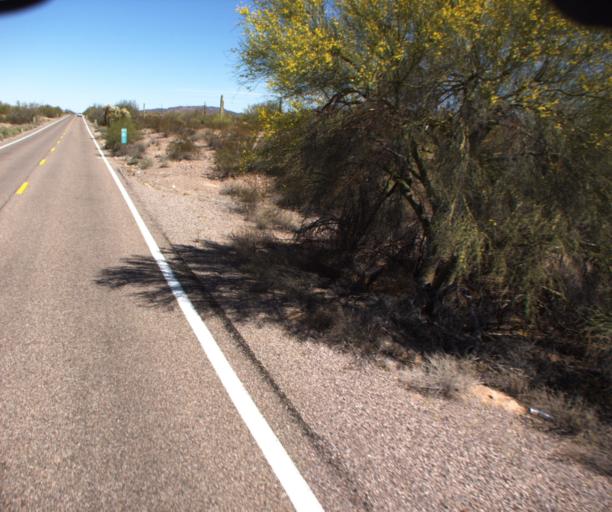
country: US
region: Arizona
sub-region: Pima County
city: Ajo
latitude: 32.1535
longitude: -112.7649
